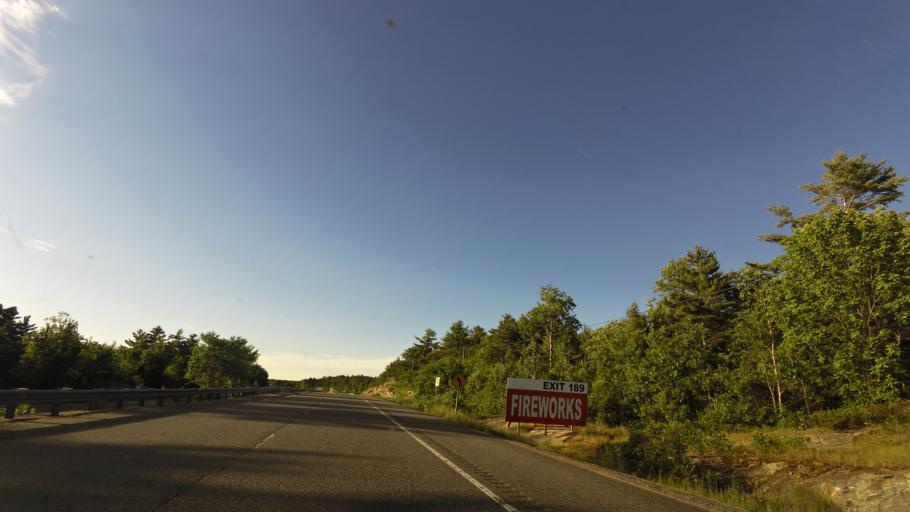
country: CA
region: Ontario
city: Midland
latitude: 44.9330
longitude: -79.7746
